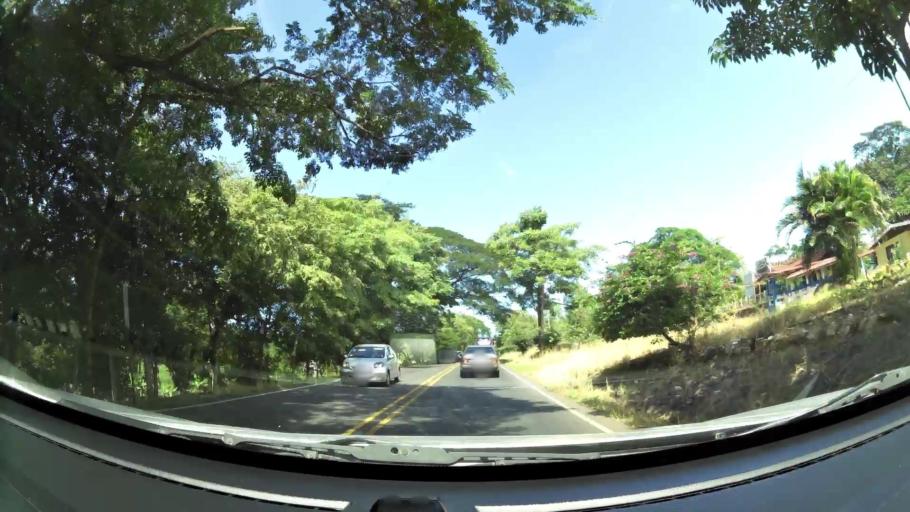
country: CR
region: Guanacaste
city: Juntas
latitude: 10.3141
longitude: -85.0438
